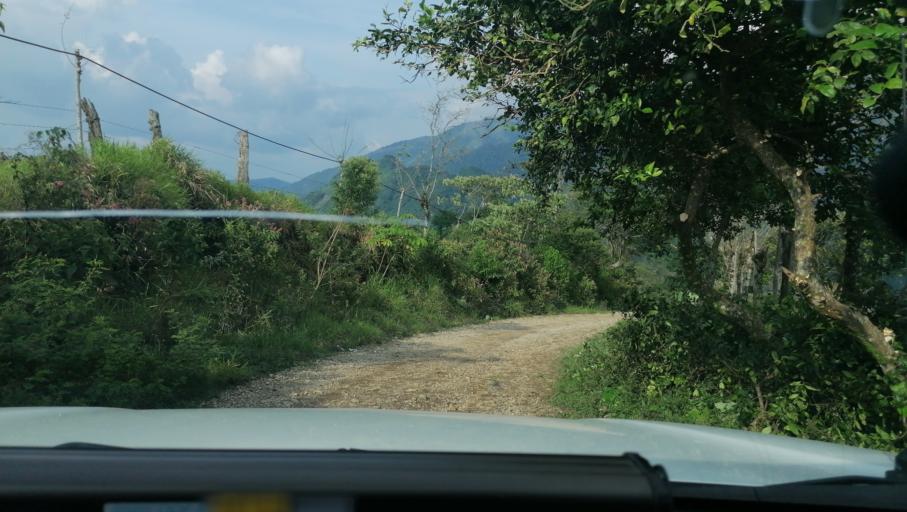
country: MX
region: Chiapas
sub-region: Tapilula
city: San Francisco Jacona
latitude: 17.3153
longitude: -93.1001
